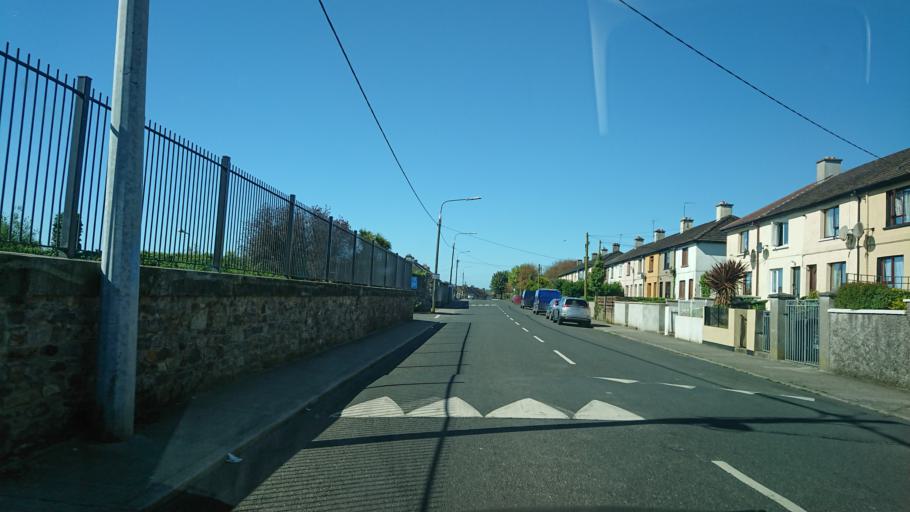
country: IE
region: Munster
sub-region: Waterford
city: Waterford
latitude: 52.2532
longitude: -7.1205
